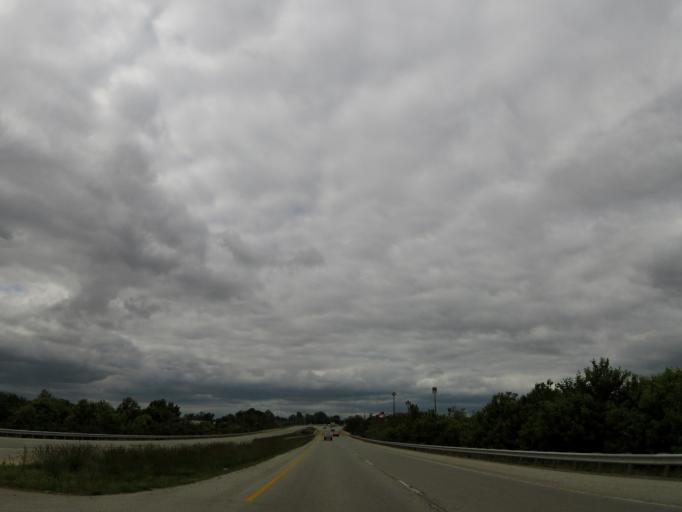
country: US
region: Kentucky
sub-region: Scott County
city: Georgetown
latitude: 38.2090
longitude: -84.5385
